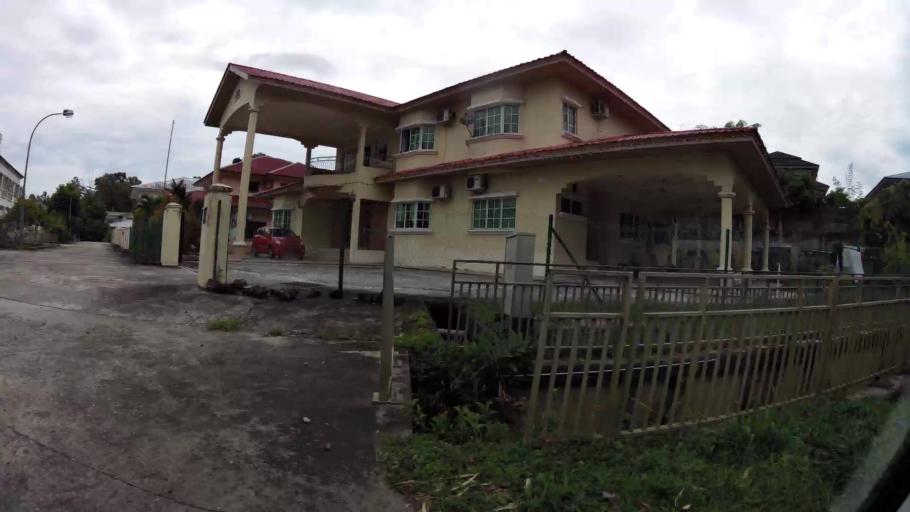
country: BN
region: Brunei and Muara
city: Bandar Seri Begawan
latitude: 4.8906
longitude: 114.9211
